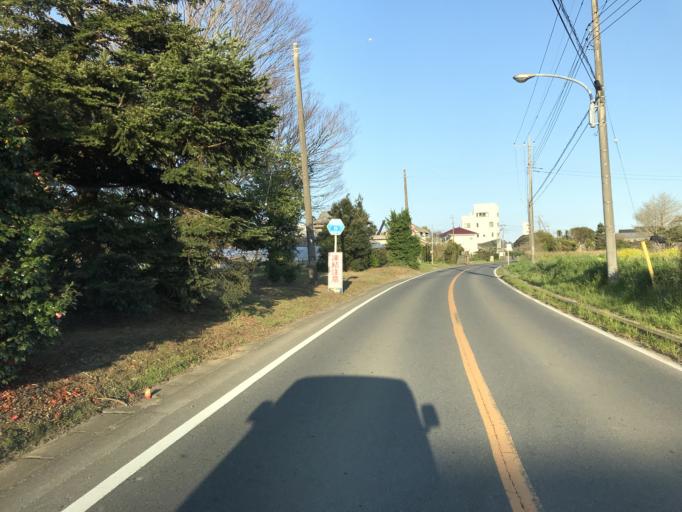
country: JP
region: Chiba
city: Yokaichiba
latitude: 35.7561
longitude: 140.5757
